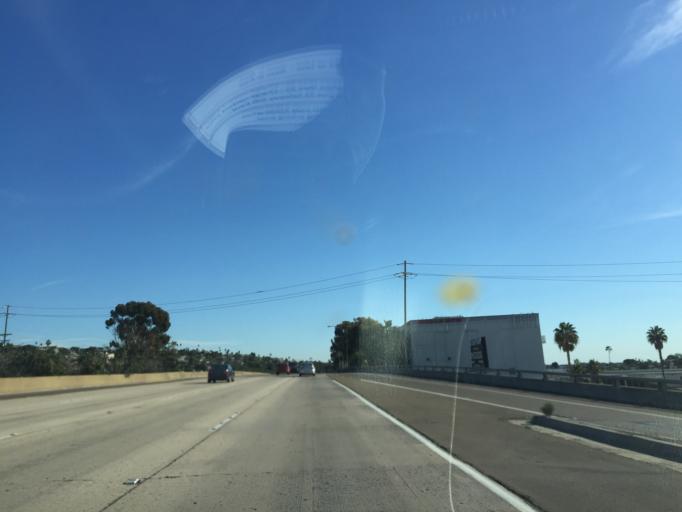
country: US
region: California
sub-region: San Diego County
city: La Jolla
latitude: 32.8076
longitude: -117.2168
